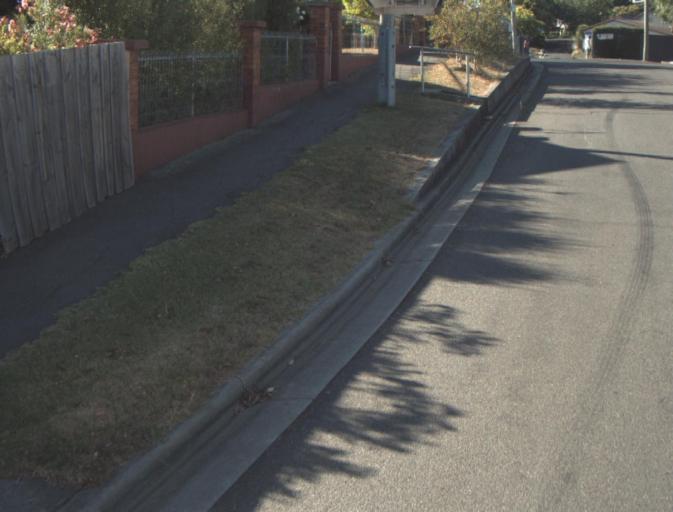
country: AU
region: Tasmania
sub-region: Launceston
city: Newnham
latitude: -41.4063
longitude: 147.1254
